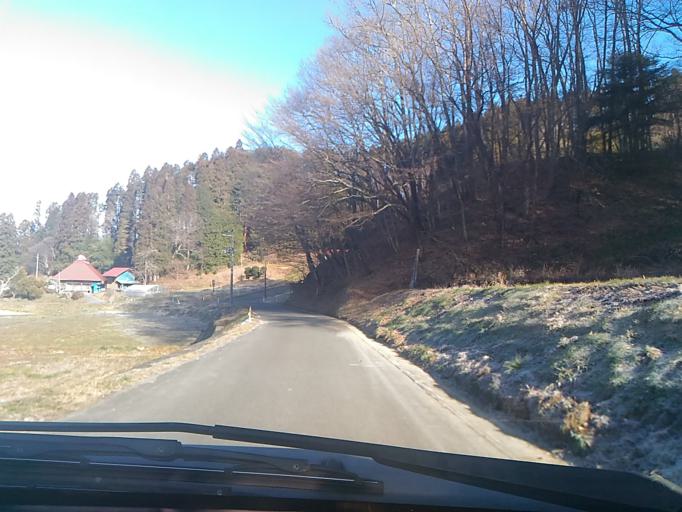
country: JP
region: Fukushima
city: Ishikawa
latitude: 37.0047
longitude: 140.5421
